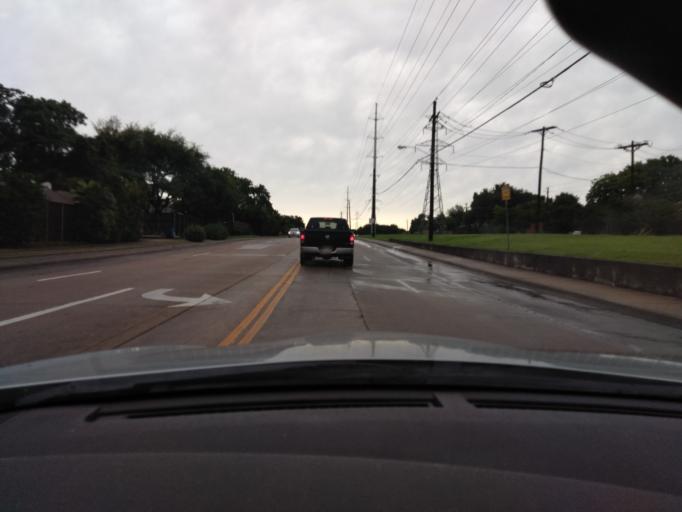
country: US
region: Texas
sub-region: Dallas County
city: Addison
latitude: 32.9786
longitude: -96.7787
